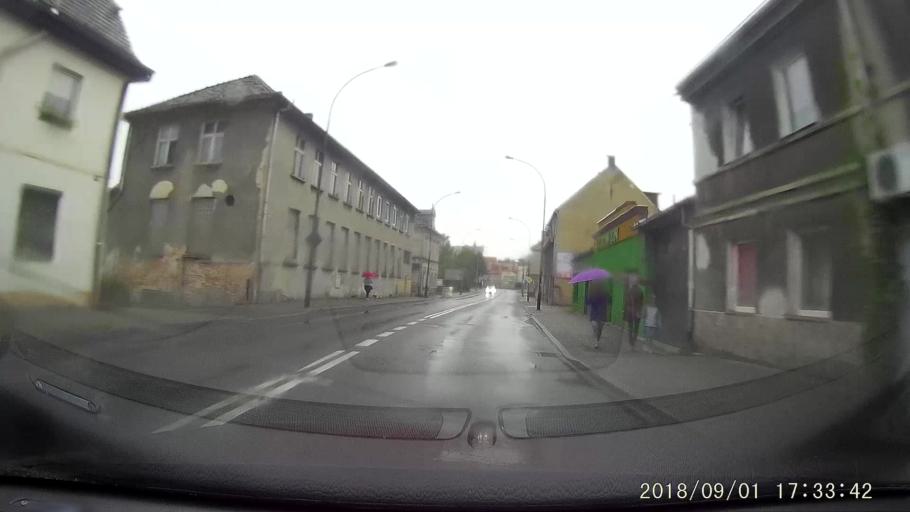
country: PL
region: Lubusz
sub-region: Powiat zaganski
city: Zagan
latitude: 51.6198
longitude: 15.3275
